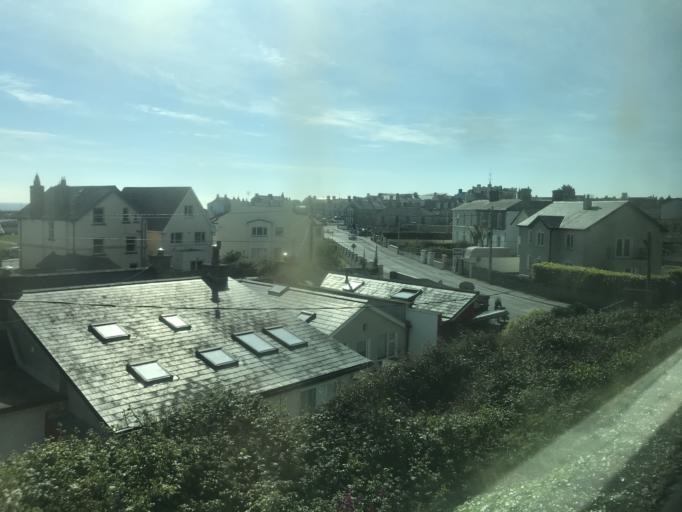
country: IE
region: Leinster
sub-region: Wicklow
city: Greystones
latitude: 53.1506
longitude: -6.0686
